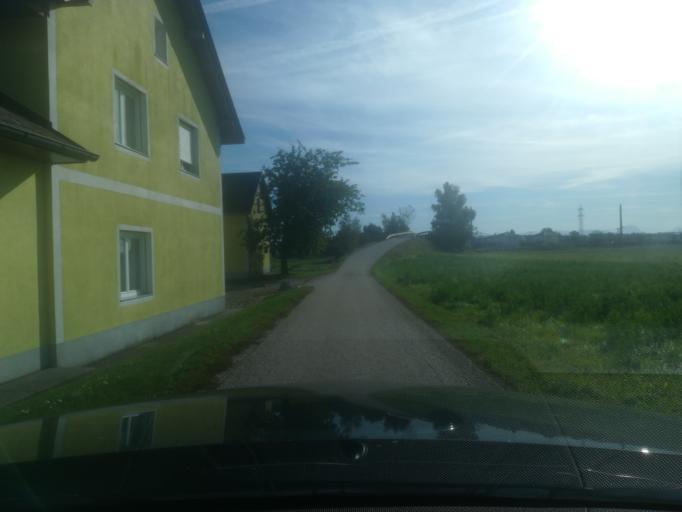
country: AT
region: Upper Austria
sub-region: Politischer Bezirk Linz-Land
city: Horsching
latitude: 48.2077
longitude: 14.1461
